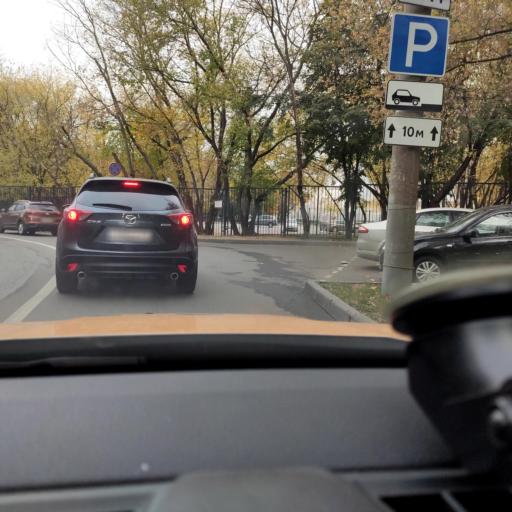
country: RU
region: Moscow
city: Tekstil'shchiki
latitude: 55.7056
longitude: 37.7379
